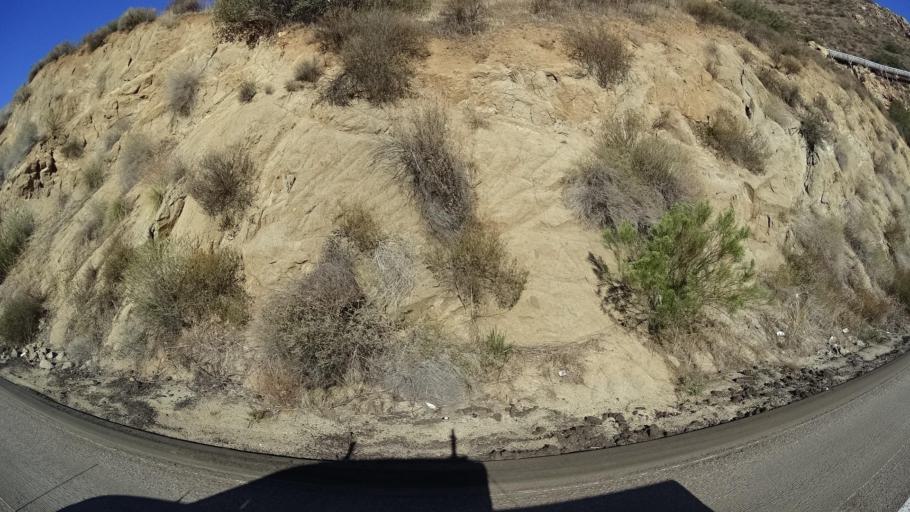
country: MX
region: Baja California
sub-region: Tecate
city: Lomas de Santa Anita
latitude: 32.6185
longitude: -116.7292
